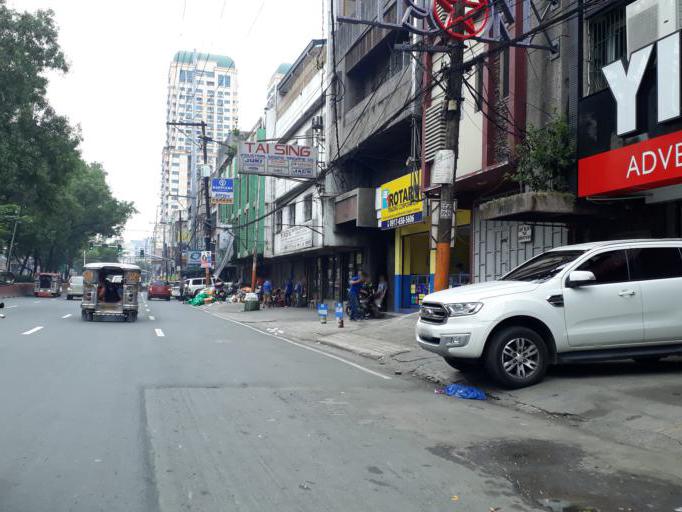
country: PH
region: Metro Manila
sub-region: City of Manila
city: Manila
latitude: 14.6150
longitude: 120.9769
